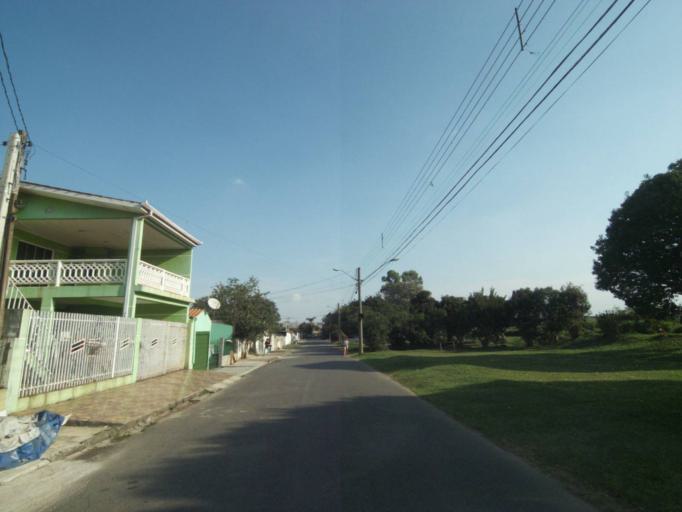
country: BR
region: Parana
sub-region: Curitiba
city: Curitiba
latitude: -25.4924
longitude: -49.3359
